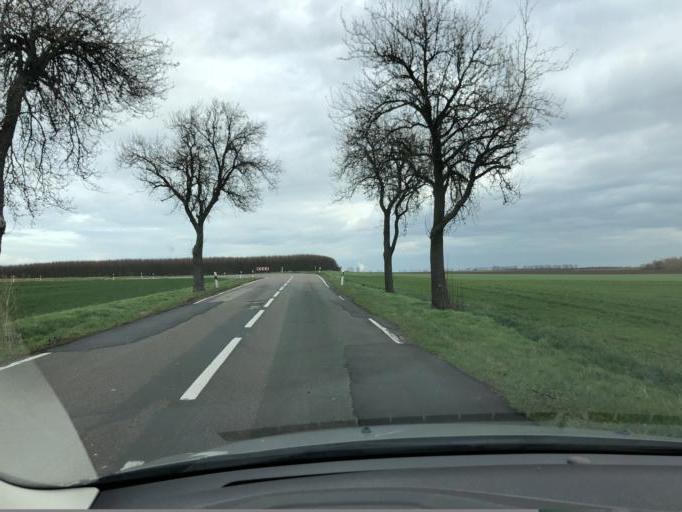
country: DE
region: Saxony-Anhalt
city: Muschwitz
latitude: 51.2040
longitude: 12.1364
